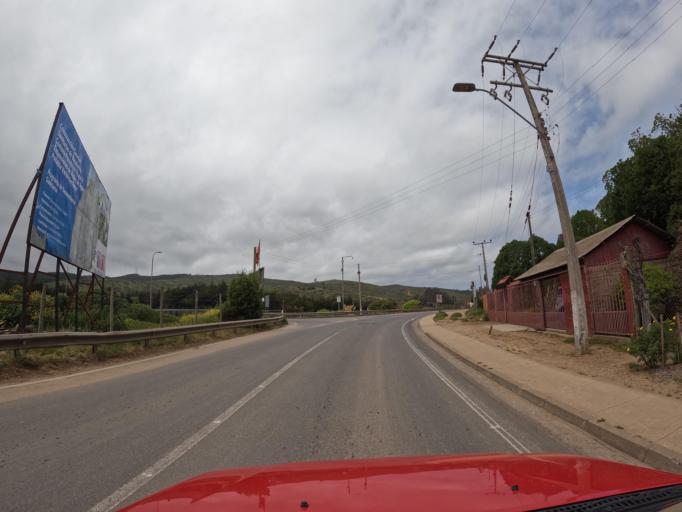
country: CL
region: O'Higgins
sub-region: Provincia de Colchagua
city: Santa Cruz
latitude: -34.6428
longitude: -72.0351
